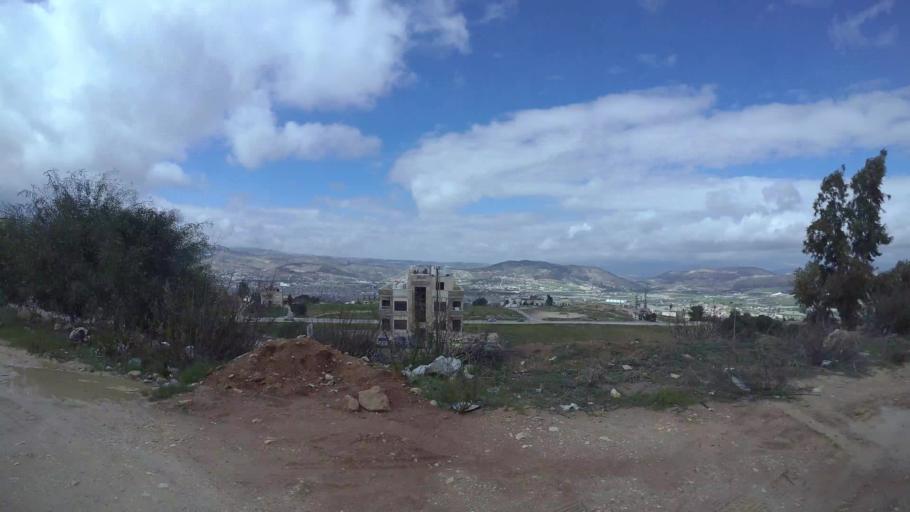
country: JO
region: Amman
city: Al Jubayhah
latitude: 32.0651
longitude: 35.8707
